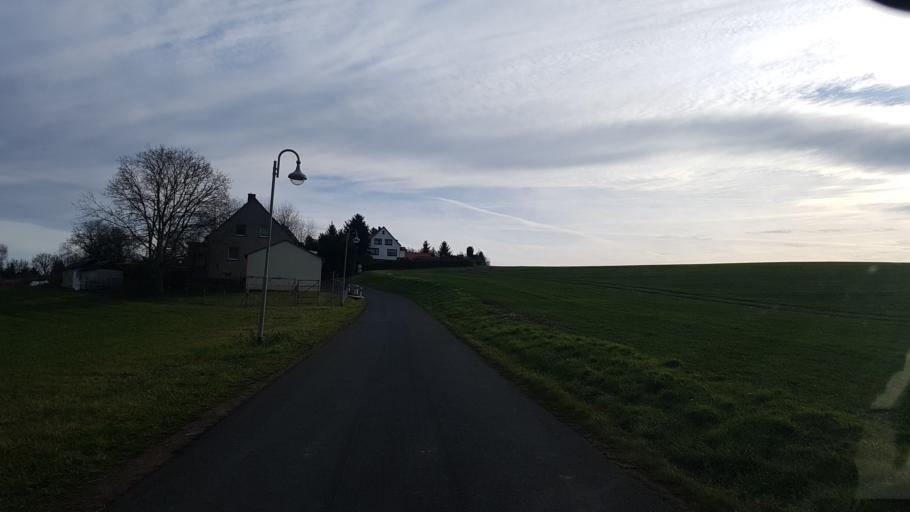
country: DE
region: Saxony
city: Ostrau
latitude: 51.1848
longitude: 13.1721
